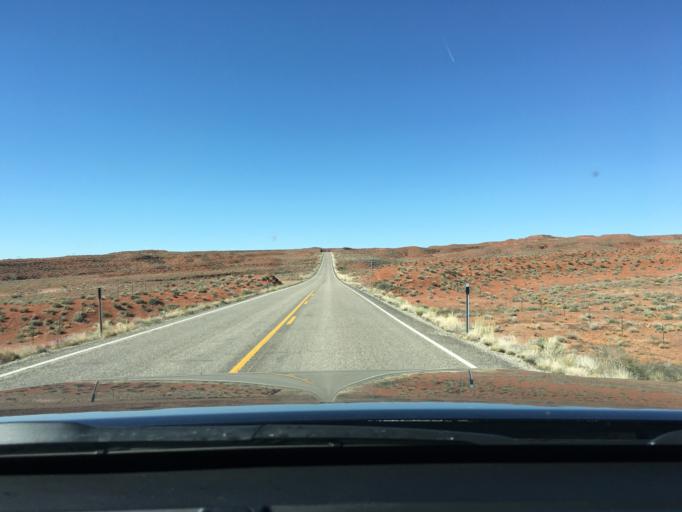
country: US
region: Utah
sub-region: San Juan County
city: Blanding
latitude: 37.2089
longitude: -109.8513
